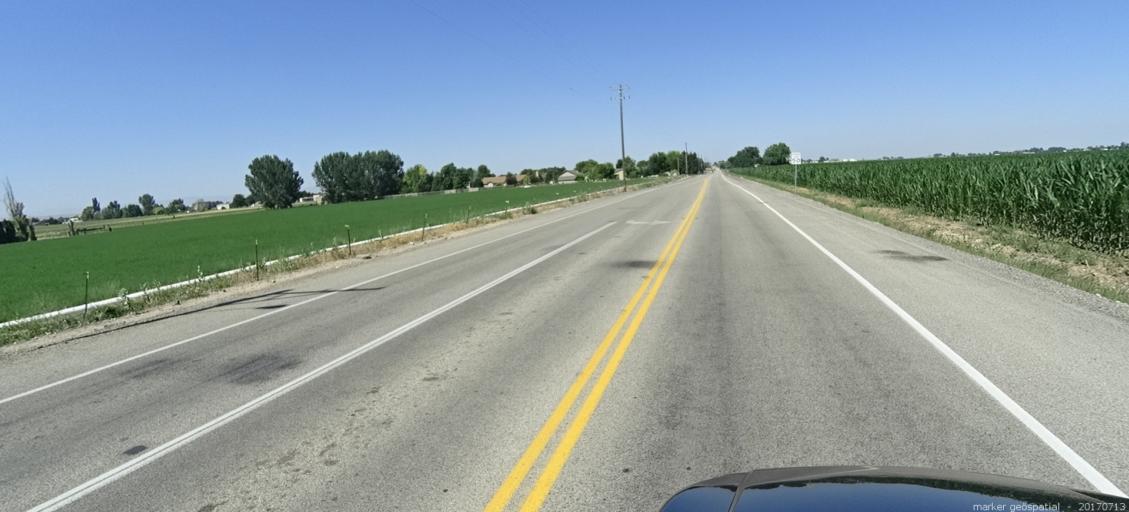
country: US
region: Idaho
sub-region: Ada County
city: Kuna
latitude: 43.5319
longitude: -116.3944
